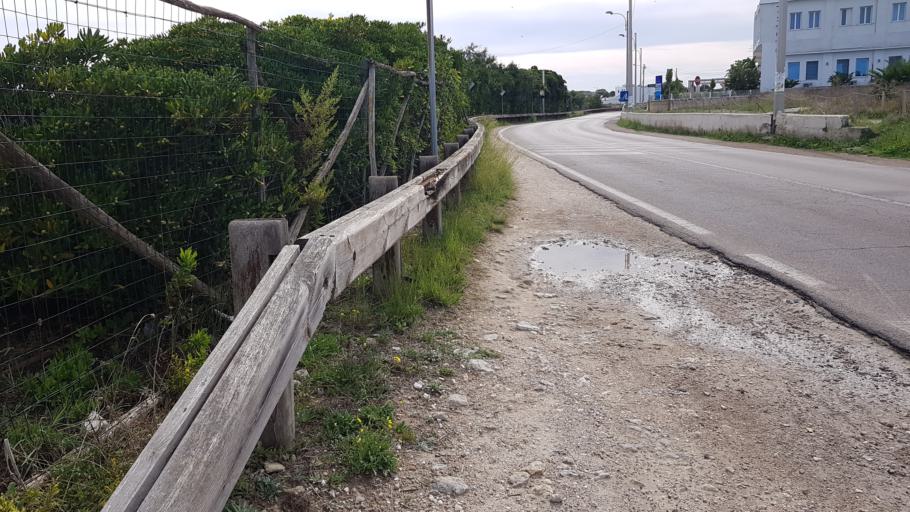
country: IT
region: Apulia
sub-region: Provincia di Lecce
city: Borgagne
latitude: 40.2873
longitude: 18.4255
